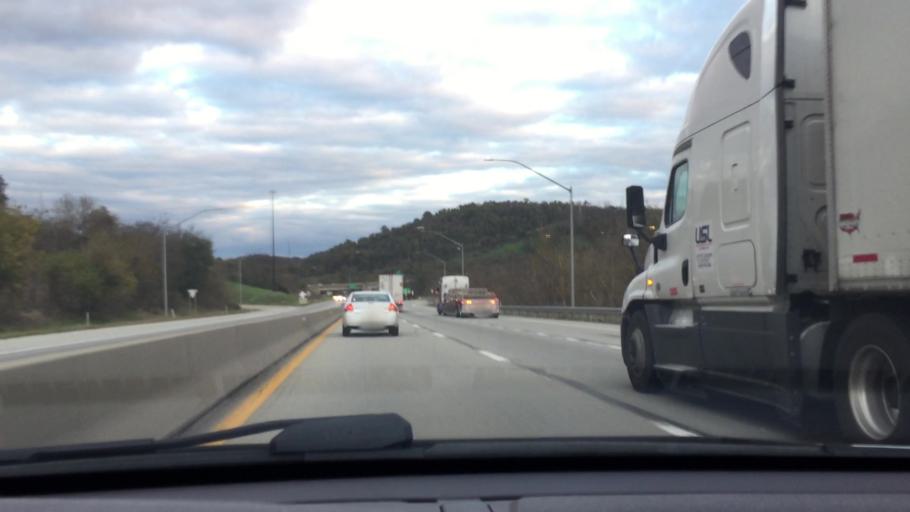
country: US
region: Pennsylvania
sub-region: Washington County
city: Charleroi
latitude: 40.1113
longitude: -79.9283
